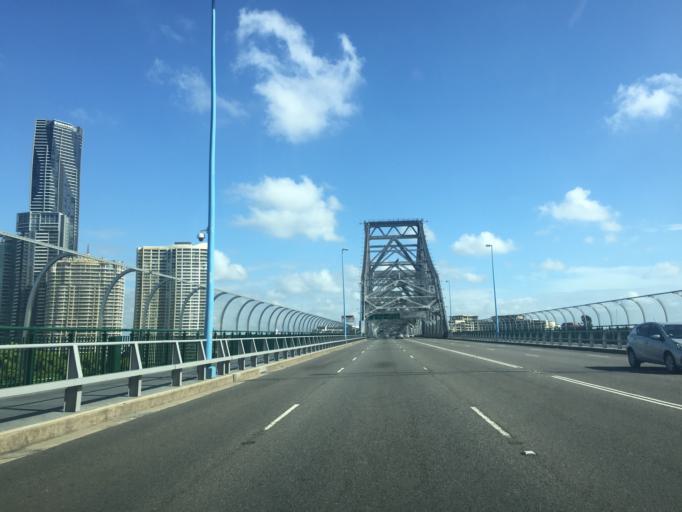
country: AU
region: Queensland
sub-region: Brisbane
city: Brisbane
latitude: -27.4670
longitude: 153.0357
